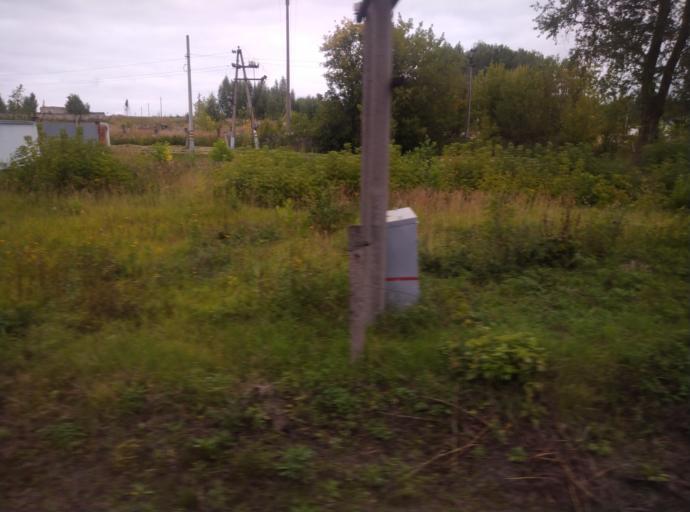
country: RU
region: Kostroma
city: Nerekhta
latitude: 57.4573
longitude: 40.5279
